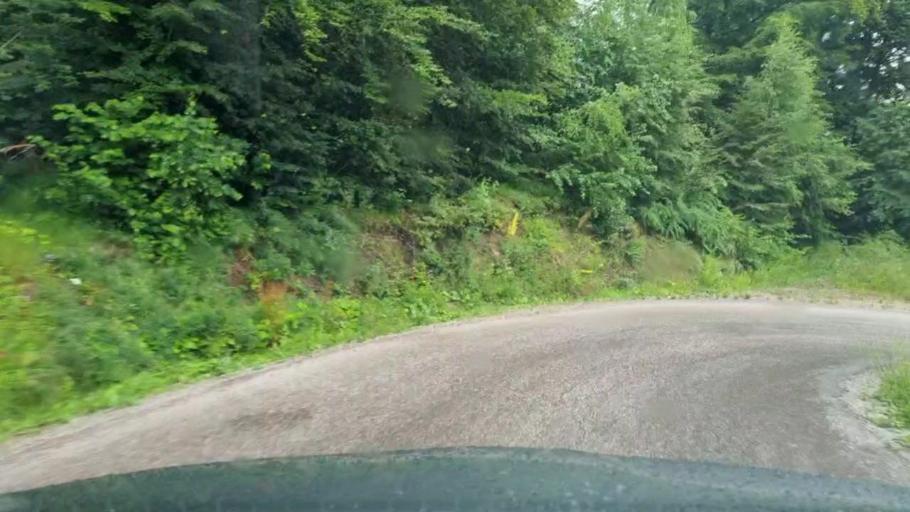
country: BA
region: Republika Srpska
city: Koran
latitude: 43.6452
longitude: 18.6125
